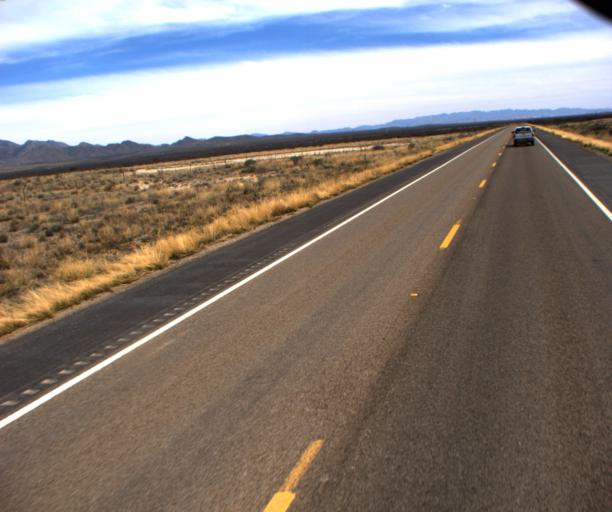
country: US
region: Arizona
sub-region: Cochise County
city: Willcox
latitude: 32.2054
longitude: -109.7718
